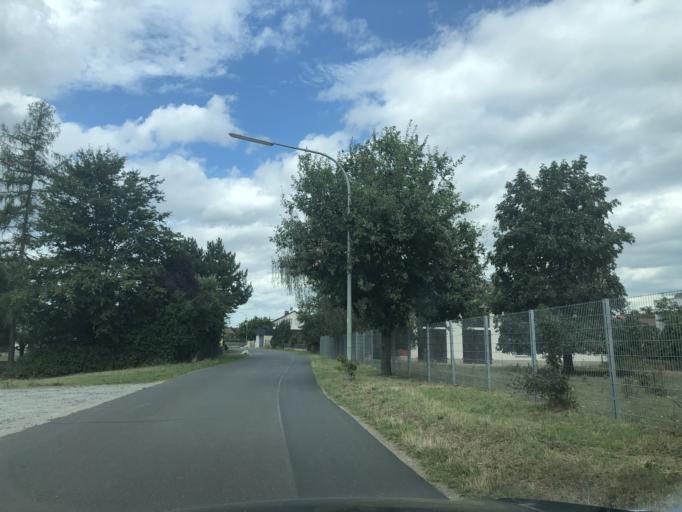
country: DE
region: Bavaria
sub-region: Upper Palatinate
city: Pressath
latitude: 49.7624
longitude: 11.9384
